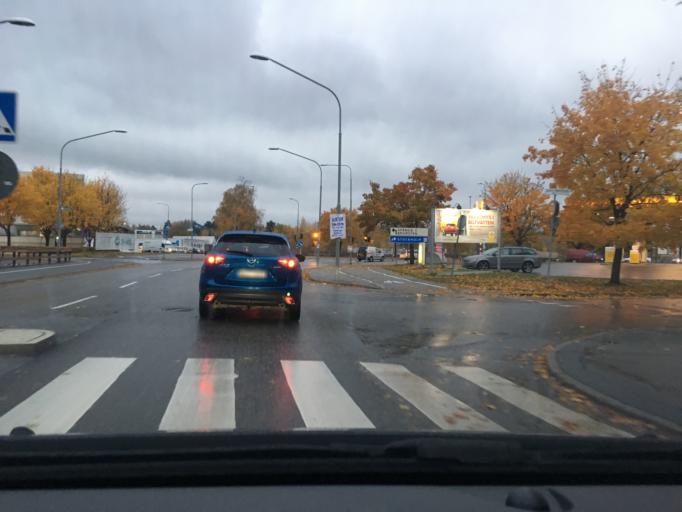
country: SE
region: Stockholm
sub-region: Stockholms Kommun
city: Kista
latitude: 59.3781
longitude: 17.9043
